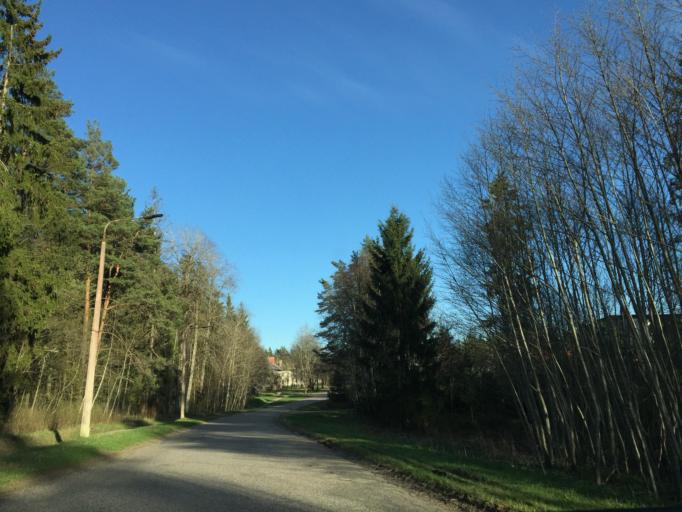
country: LV
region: Valkas Rajons
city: Valka
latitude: 57.7882
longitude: 25.9920
